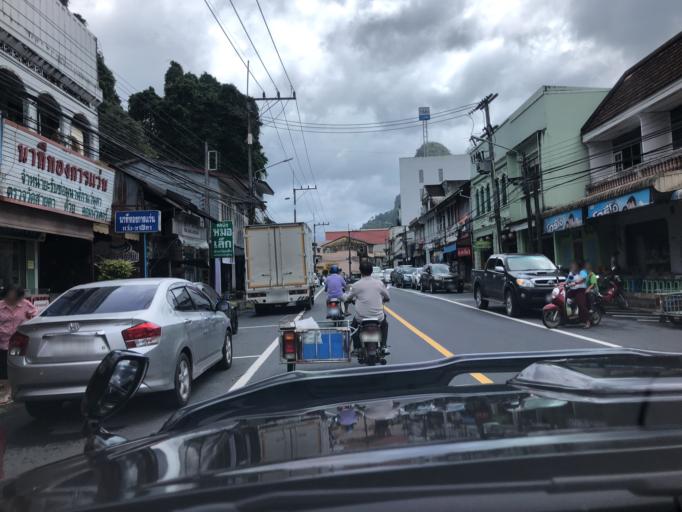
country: TH
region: Phangnga
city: Phang Nga
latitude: 8.4663
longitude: 98.5311
